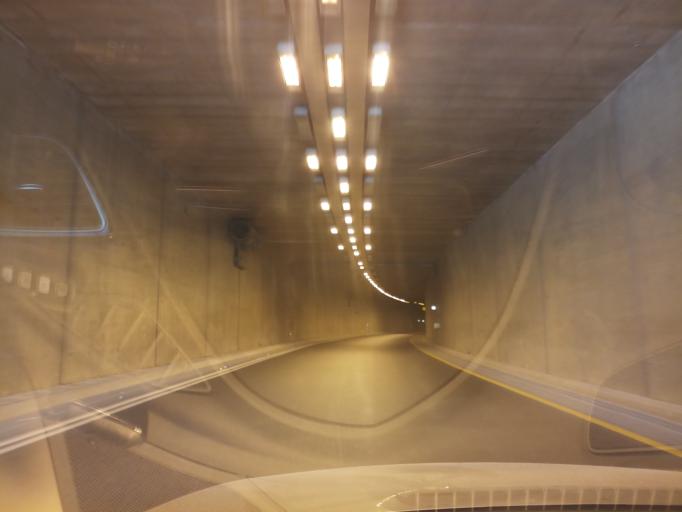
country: IL
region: Jerusalem
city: Jerusalem
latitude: 31.7648
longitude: 35.1932
